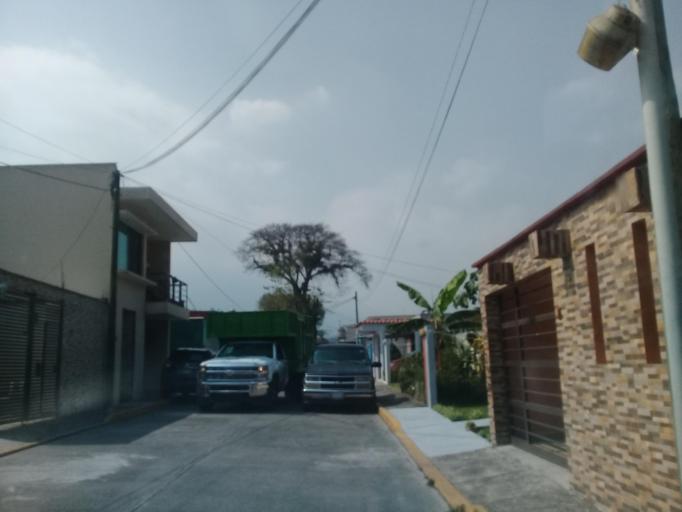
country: MX
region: Veracruz
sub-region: Mariano Escobedo
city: Palmira
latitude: 18.8774
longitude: -97.1032
